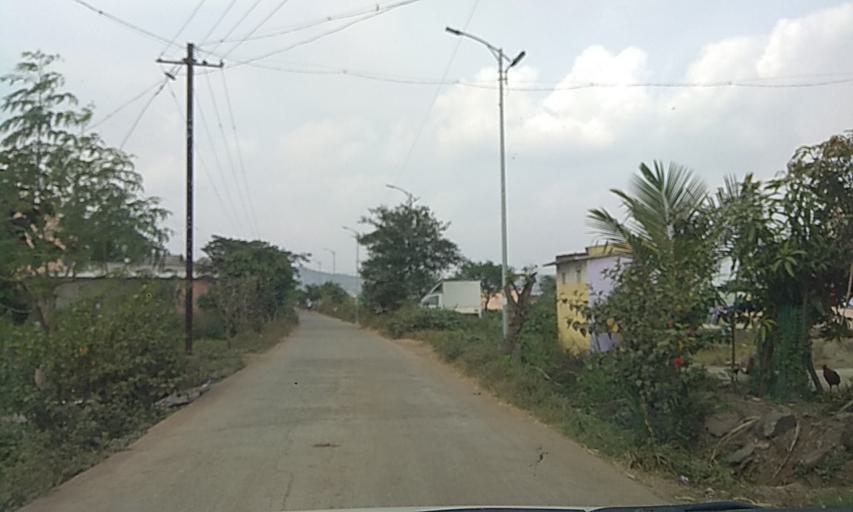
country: IN
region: Maharashtra
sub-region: Pune Division
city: Pimpri
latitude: 18.5778
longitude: 73.7085
